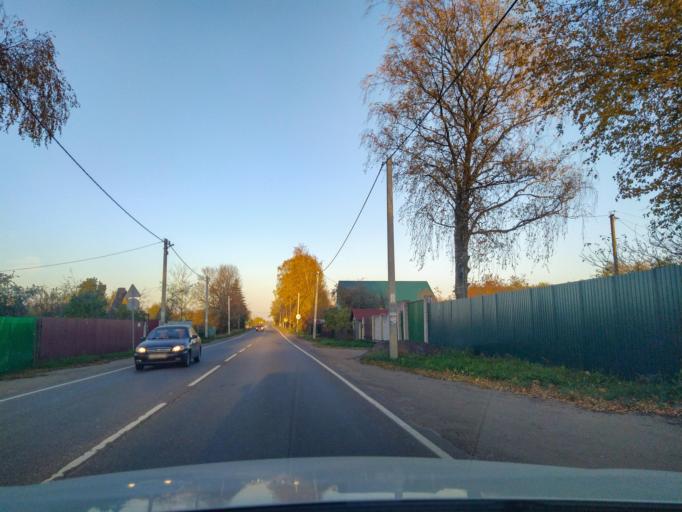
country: RU
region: Leningrad
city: Kobrinskoye
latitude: 59.4763
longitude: 30.1313
